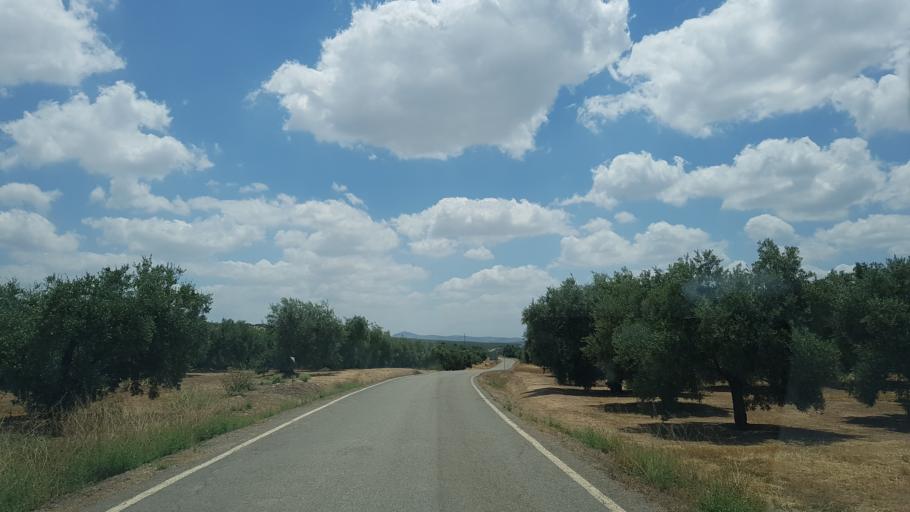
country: ES
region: Andalusia
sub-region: Province of Cordoba
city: Cabra
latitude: 37.5179
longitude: -4.4449
